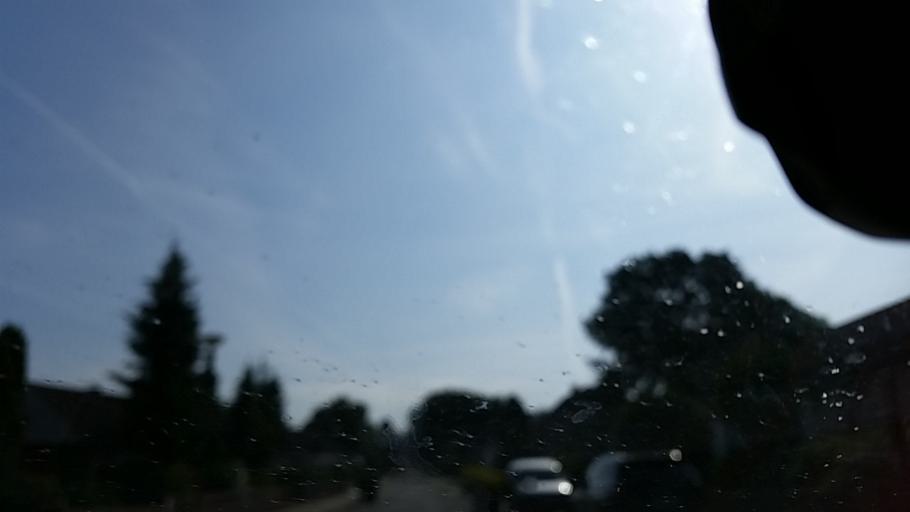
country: DE
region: Lower Saxony
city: Ruhen
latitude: 52.4569
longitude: 10.8446
